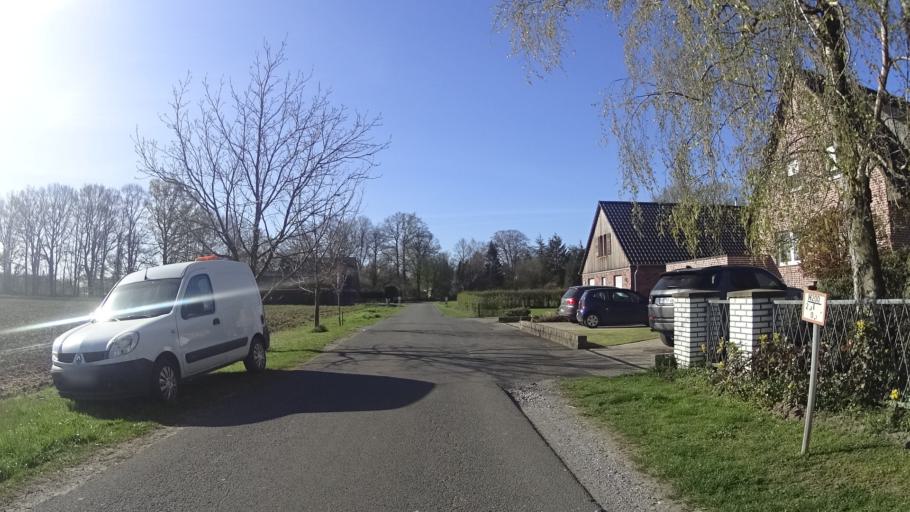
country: DE
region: North Rhine-Westphalia
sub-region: Regierungsbezirk Munster
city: Greven
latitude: 52.0374
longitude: 7.6261
